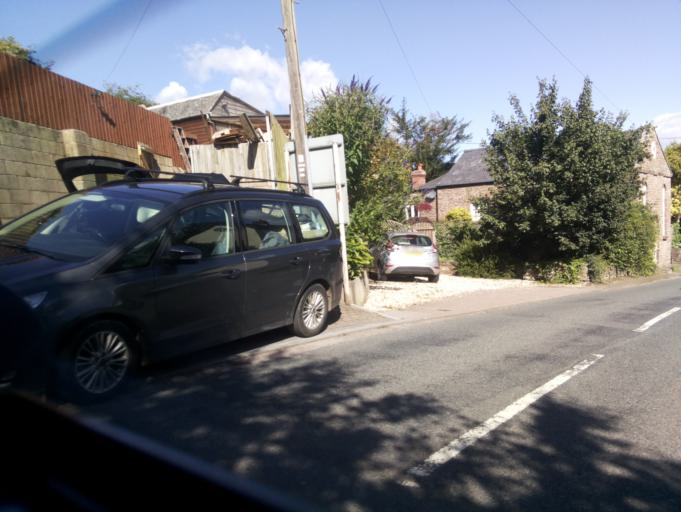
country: GB
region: England
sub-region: Herefordshire
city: Linton
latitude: 51.9401
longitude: -2.5259
